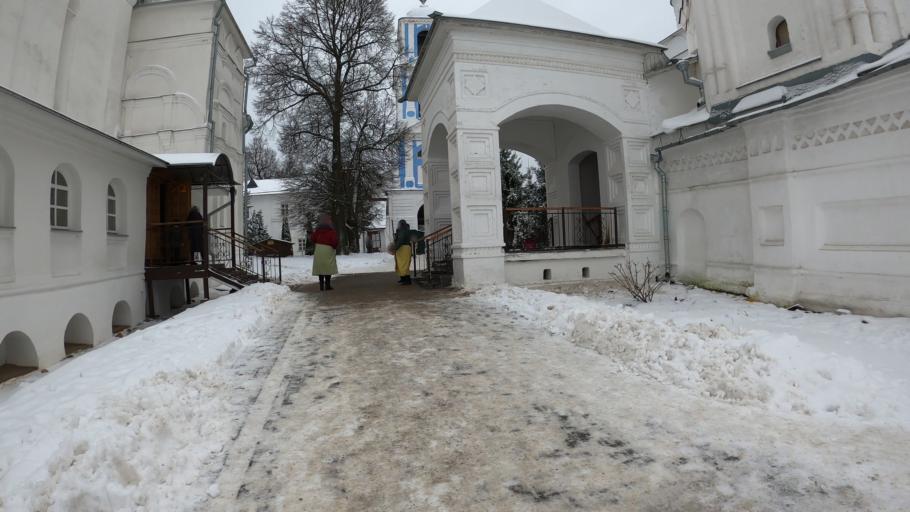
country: RU
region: Jaroslavl
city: Pereslavl'-Zalesskiy
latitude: 56.7612
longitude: 38.8589
